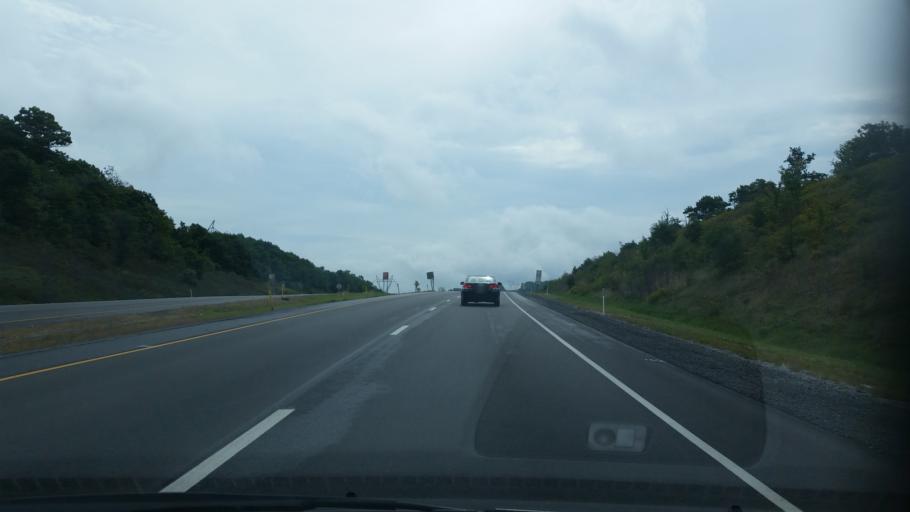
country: US
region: Pennsylvania
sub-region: Centre County
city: Philipsburg
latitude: 40.8428
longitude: -78.1345
